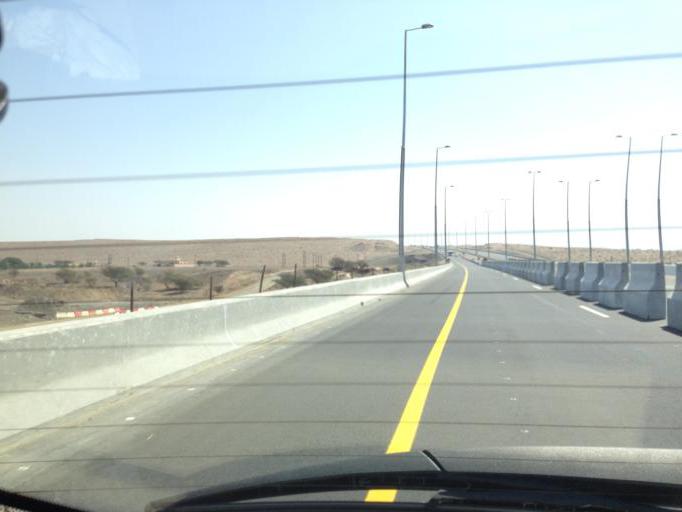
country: OM
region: Al Batinah
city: Rustaq
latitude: 23.5197
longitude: 57.6207
